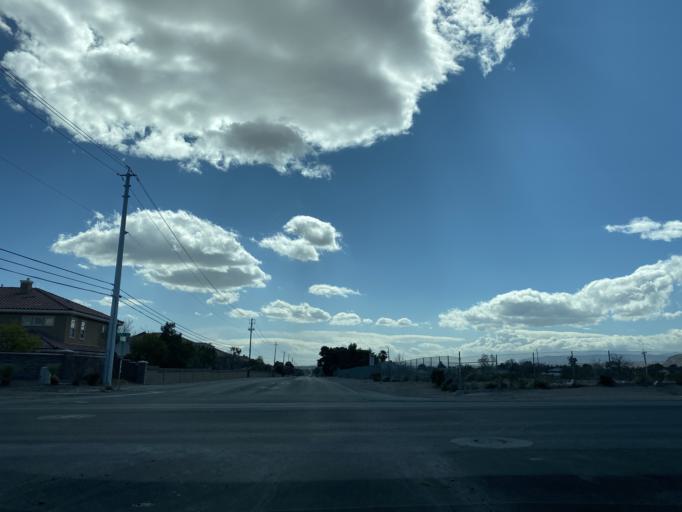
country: US
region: Nevada
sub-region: Clark County
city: Summerlin South
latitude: 36.2629
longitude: -115.2885
